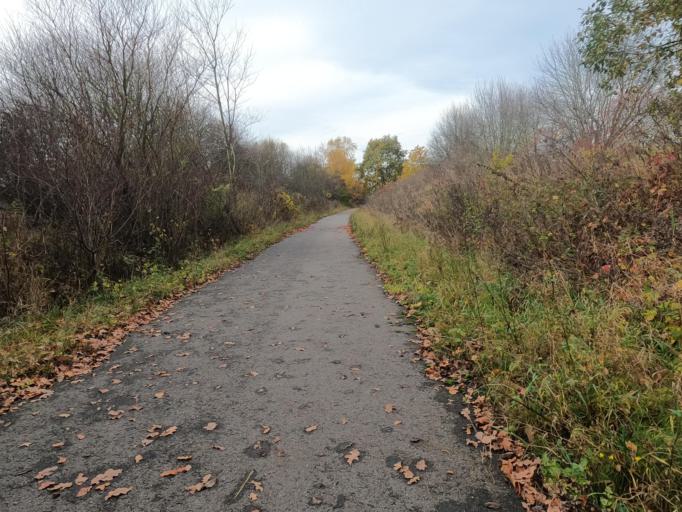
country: PL
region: Pomeranian Voivodeship
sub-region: Powiat starogardzki
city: Starogard Gdanski
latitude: 53.9732
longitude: 18.5023
